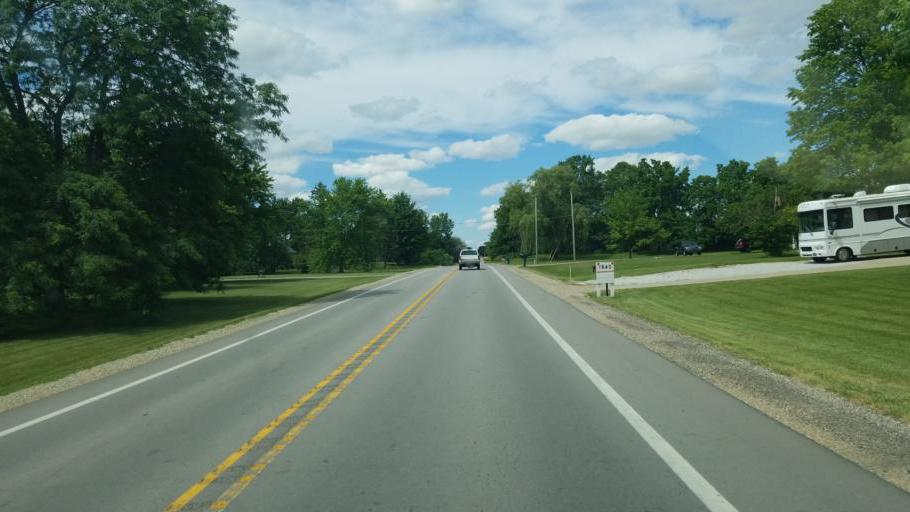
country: US
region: Michigan
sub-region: Eaton County
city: Charlotte
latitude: 42.5916
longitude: -84.8361
